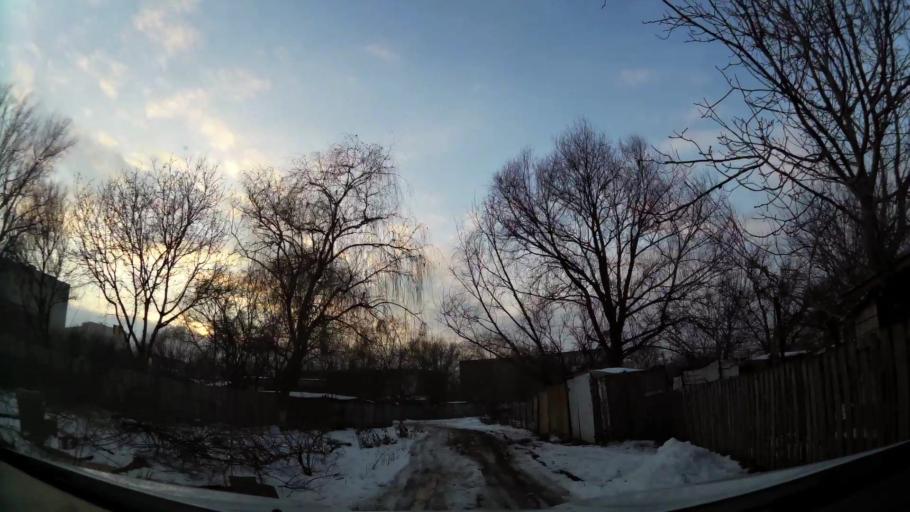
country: RO
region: Ilfov
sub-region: Comuna Popesti-Leordeni
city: Popesti-Leordeni
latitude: 44.3655
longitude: 26.1967
